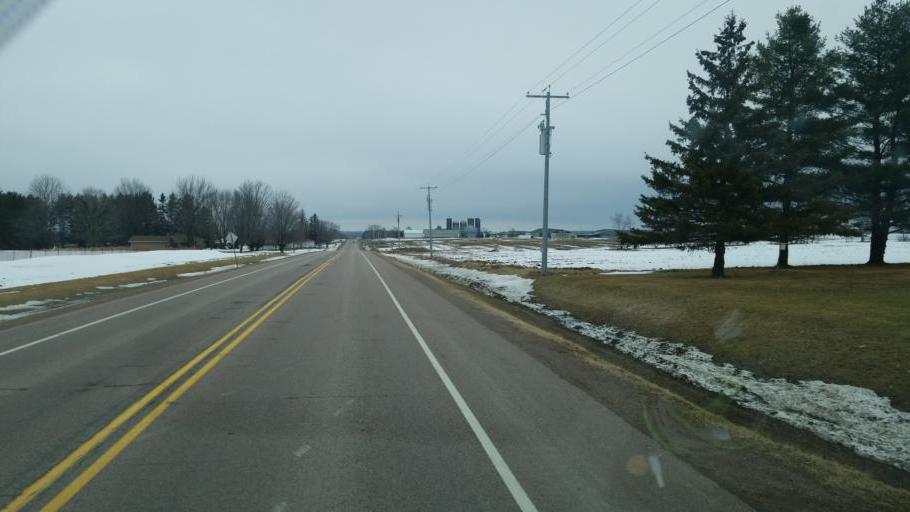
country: US
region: Wisconsin
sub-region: Wood County
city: Marshfield
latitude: 44.6357
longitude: -90.2183
